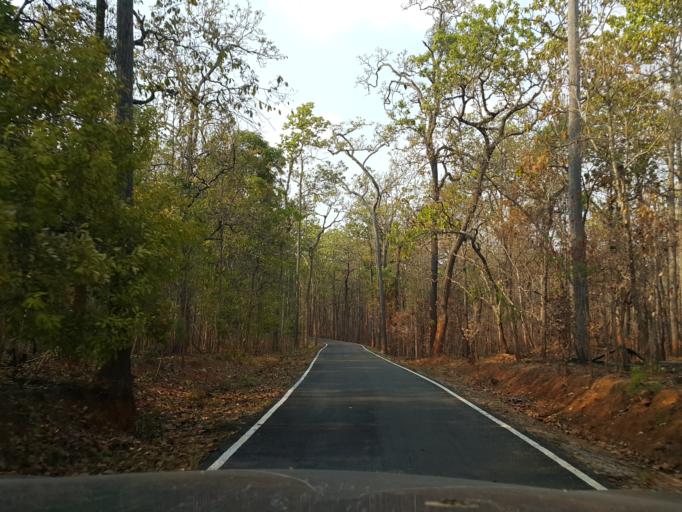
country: TH
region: Lamphun
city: Li
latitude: 17.6355
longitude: 98.8800
